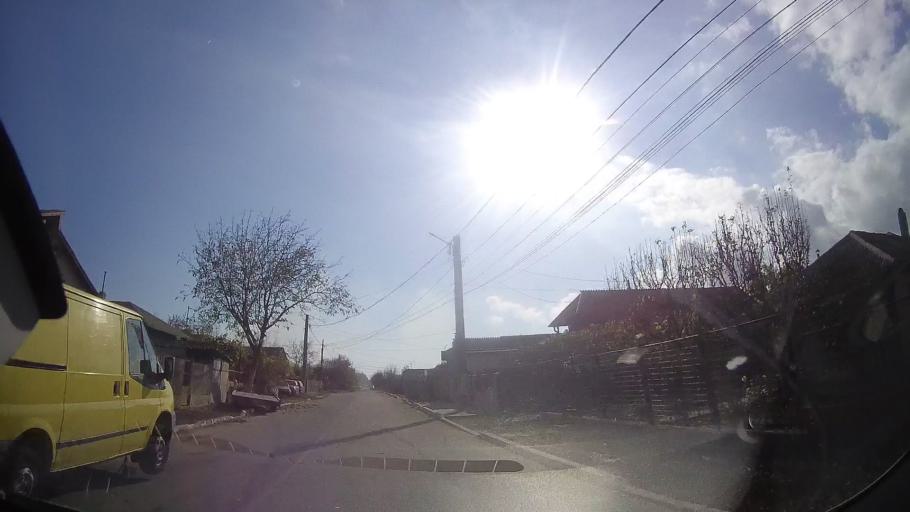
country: RO
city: Eforie Sud
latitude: 44.0125
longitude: 28.6438
